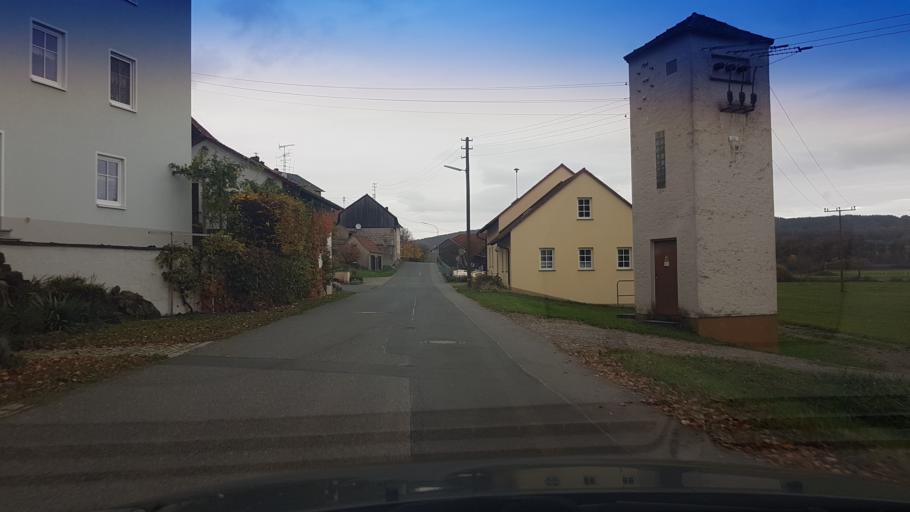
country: DE
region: Bavaria
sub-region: Upper Franconia
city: Rattelsdorf
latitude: 50.0473
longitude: 10.8717
